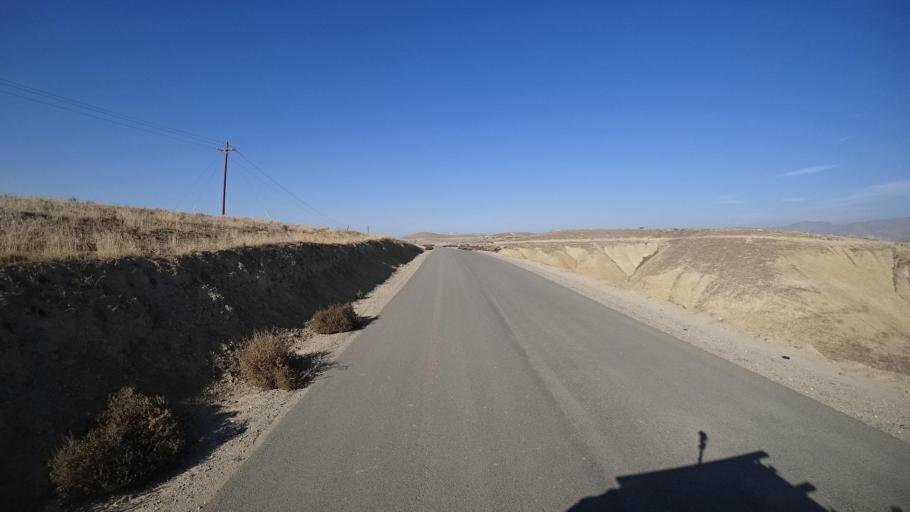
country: US
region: California
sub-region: Kern County
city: Oildale
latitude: 35.4779
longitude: -118.8764
